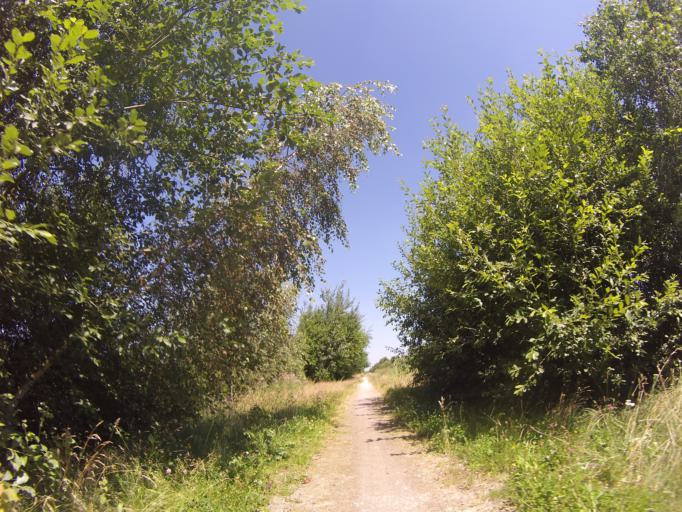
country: NL
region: Drenthe
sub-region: Gemeente Emmen
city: Klazienaveen
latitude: 52.7349
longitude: 7.0234
